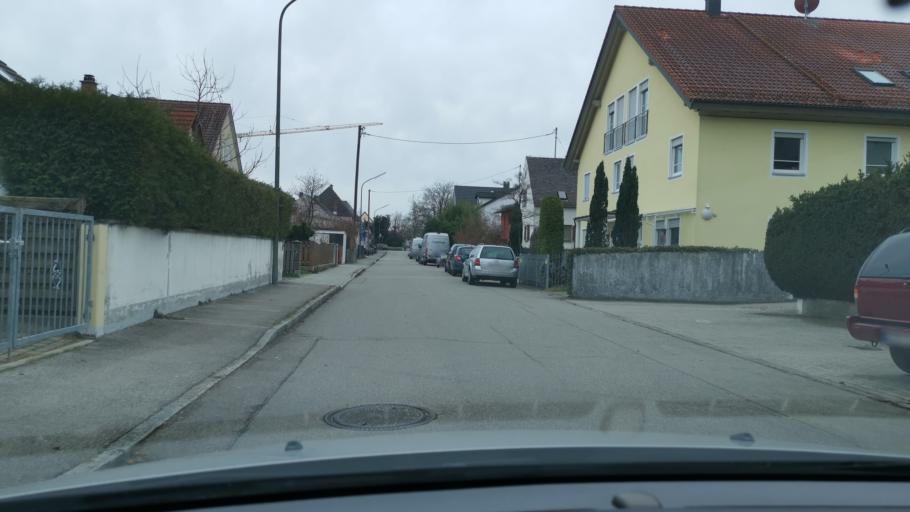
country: DE
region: Bavaria
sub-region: Upper Bavaria
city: Unterschleissheim
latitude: 48.2835
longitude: 11.5763
